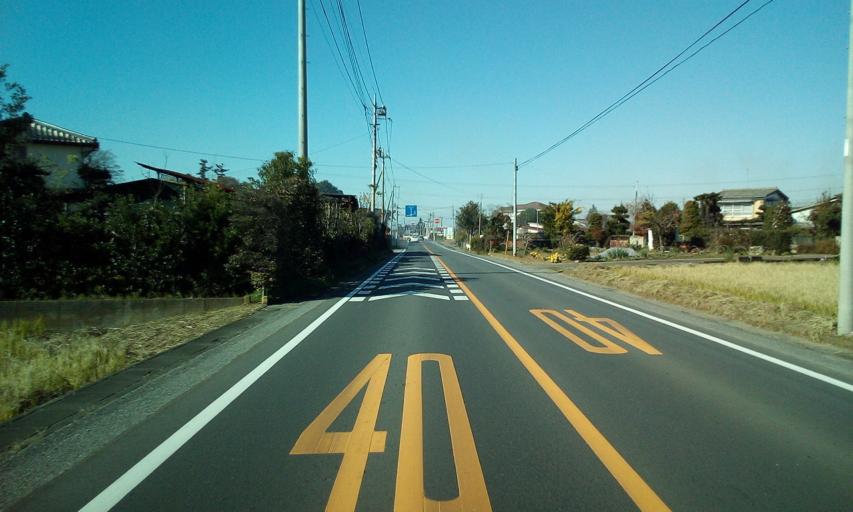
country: JP
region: Ibaraki
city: Sakai
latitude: 36.0492
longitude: 139.7802
